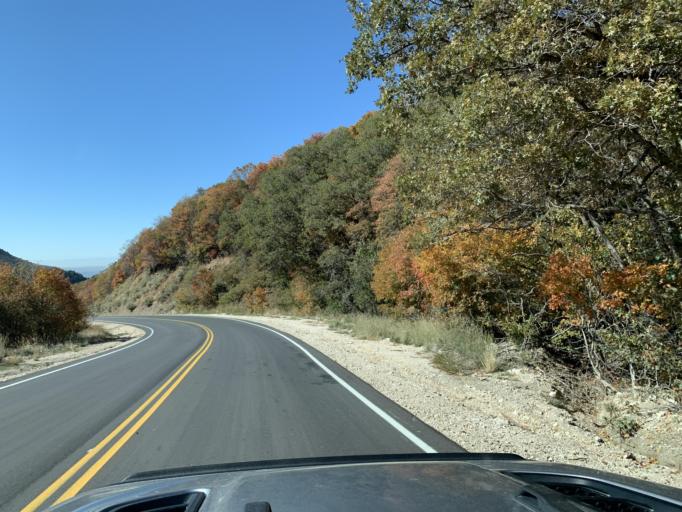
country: US
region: Utah
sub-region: Weber County
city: Liberty
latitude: 41.3201
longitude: -111.9033
